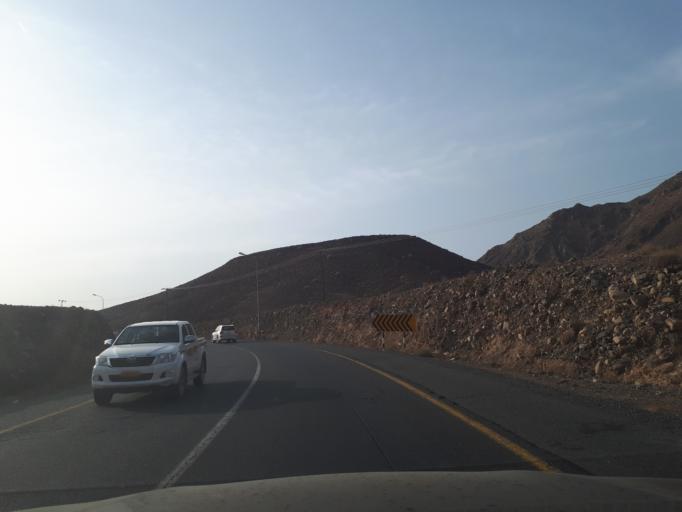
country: OM
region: Muhafazat ad Dakhiliyah
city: Sufalat Sama'il
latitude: 23.1854
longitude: 58.0962
